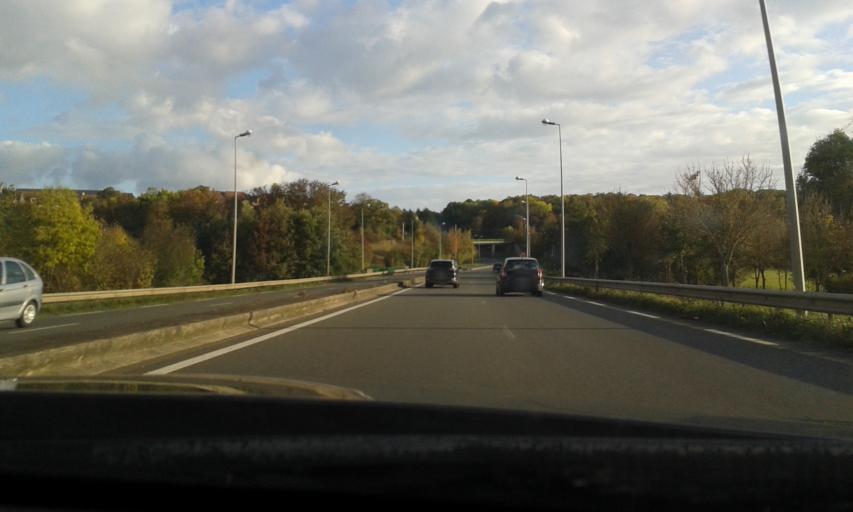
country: FR
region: Centre
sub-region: Departement d'Eure-et-Loir
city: Vernouillet
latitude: 48.7168
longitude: 1.3514
